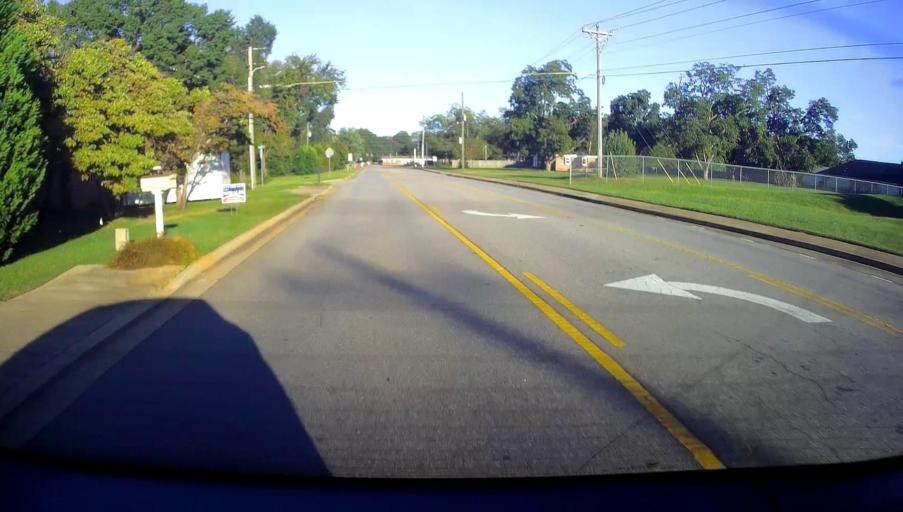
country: US
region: Georgia
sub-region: Houston County
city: Centerville
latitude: 32.6349
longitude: -83.6927
